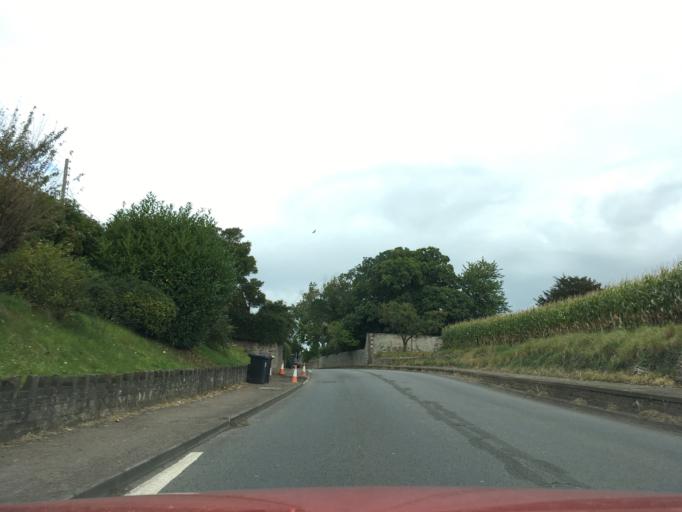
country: GB
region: England
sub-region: Gloucestershire
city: Mitcheldean
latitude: 51.8262
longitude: -2.4138
